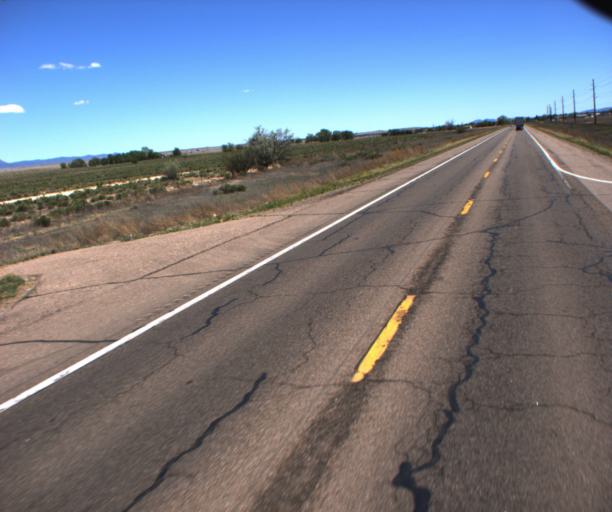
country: US
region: Arizona
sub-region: Yavapai County
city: Chino Valley
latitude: 34.8124
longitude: -112.4526
